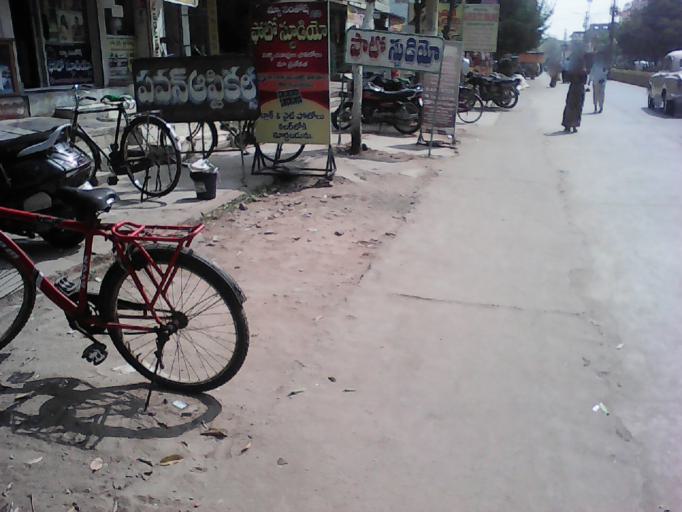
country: IN
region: Andhra Pradesh
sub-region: Guntur
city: Bhattiprolu
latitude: 16.2341
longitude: 80.6503
